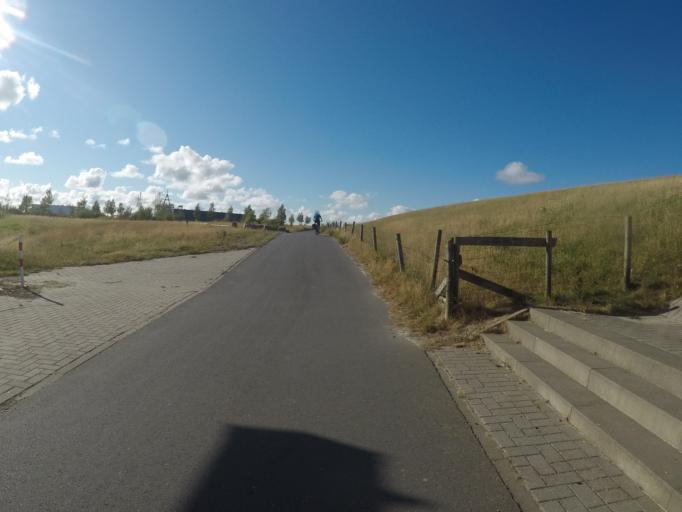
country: DE
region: Lower Saxony
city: Cuxhaven
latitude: 53.8366
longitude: 8.7690
